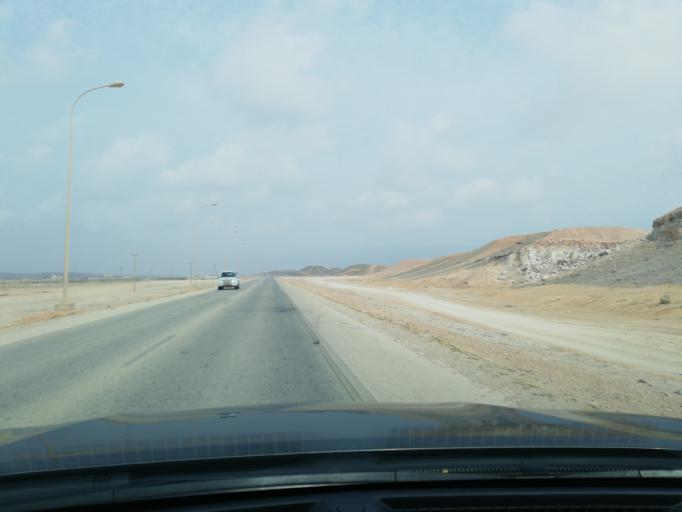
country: OM
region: Zufar
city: Salalah
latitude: 16.9466
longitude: 53.9471
